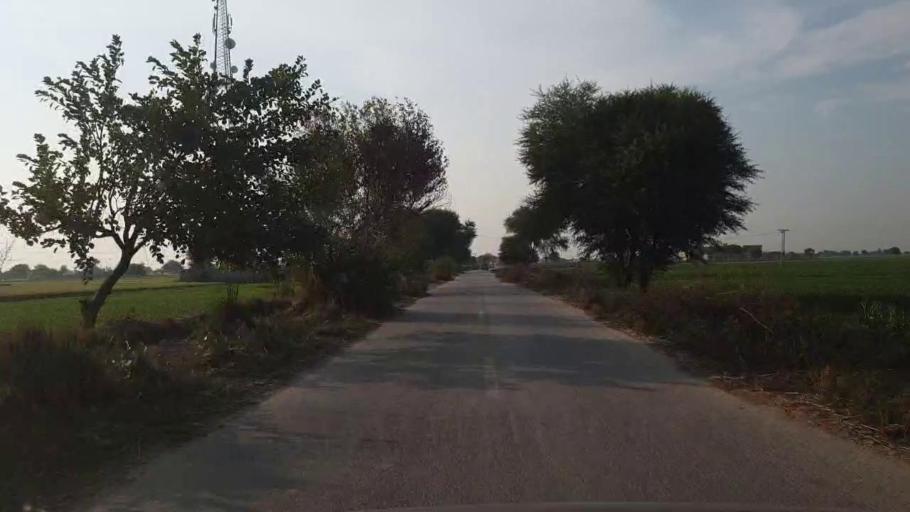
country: PK
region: Sindh
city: Shahpur Chakar
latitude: 26.1612
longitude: 68.6344
